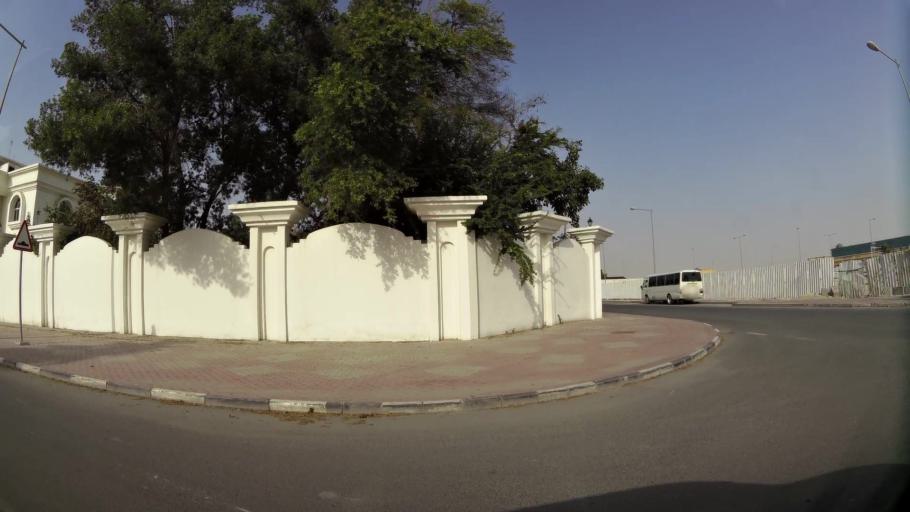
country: QA
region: Baladiyat ar Rayyan
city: Ar Rayyan
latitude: 25.2343
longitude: 51.4441
